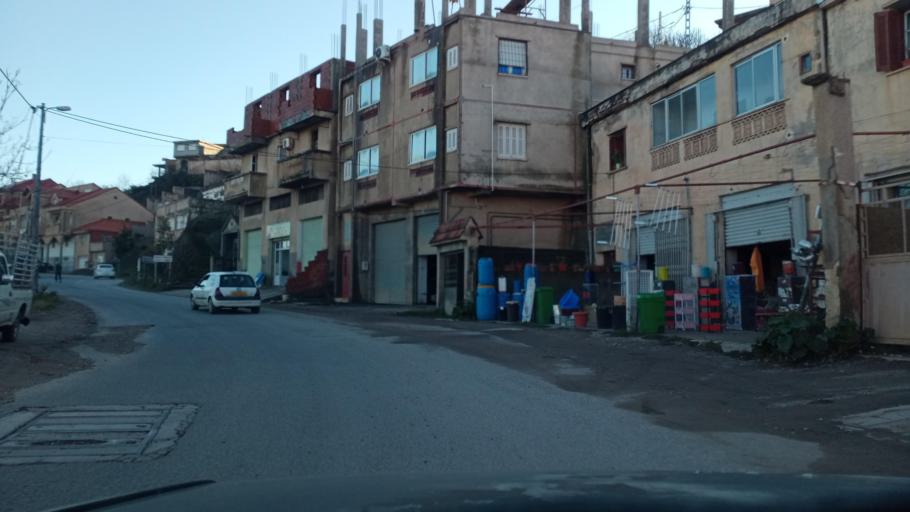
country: DZ
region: Tizi Ouzou
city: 'Ain el Hammam
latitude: 36.5606
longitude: 4.3240
